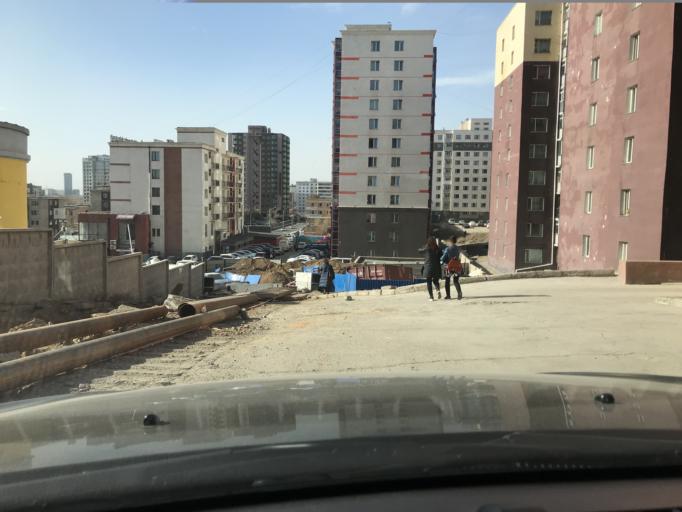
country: MN
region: Ulaanbaatar
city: Ulaanbaatar
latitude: 47.9215
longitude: 106.9546
